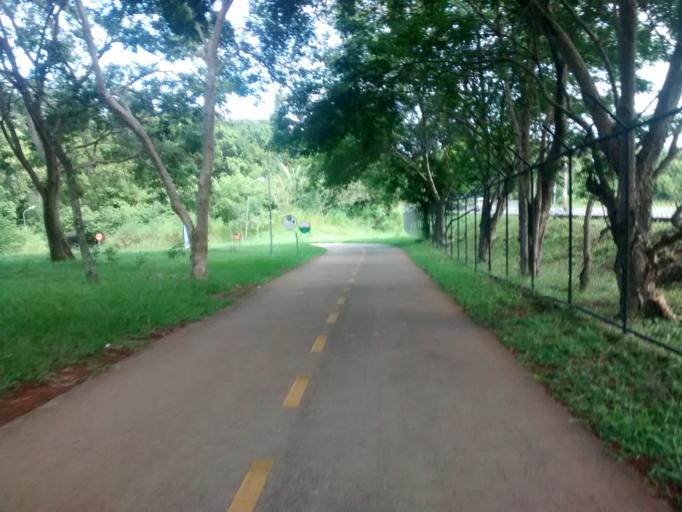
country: BR
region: Federal District
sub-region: Brasilia
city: Brasilia
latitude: -15.7445
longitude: -47.8831
